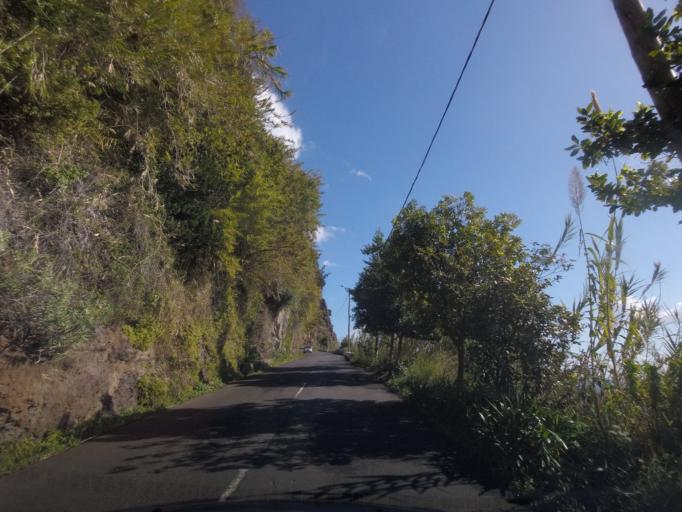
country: PT
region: Madeira
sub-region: Calheta
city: Estreito da Calheta
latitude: 32.7337
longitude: -17.2044
